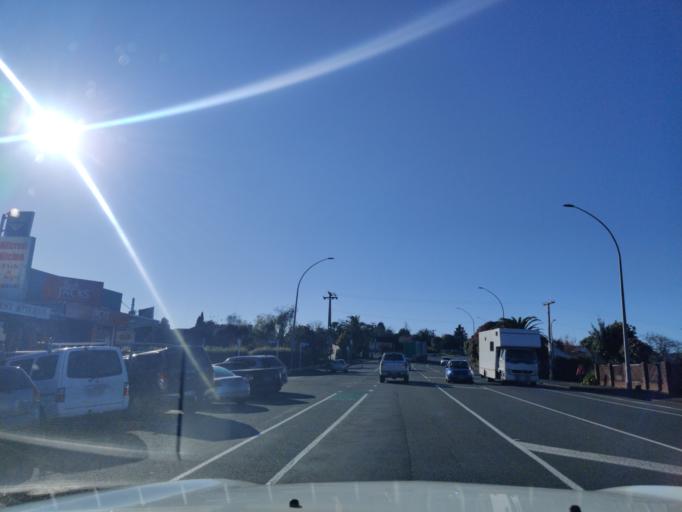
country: NZ
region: Waikato
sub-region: Hamilton City
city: Hamilton
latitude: -37.7976
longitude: 175.3103
